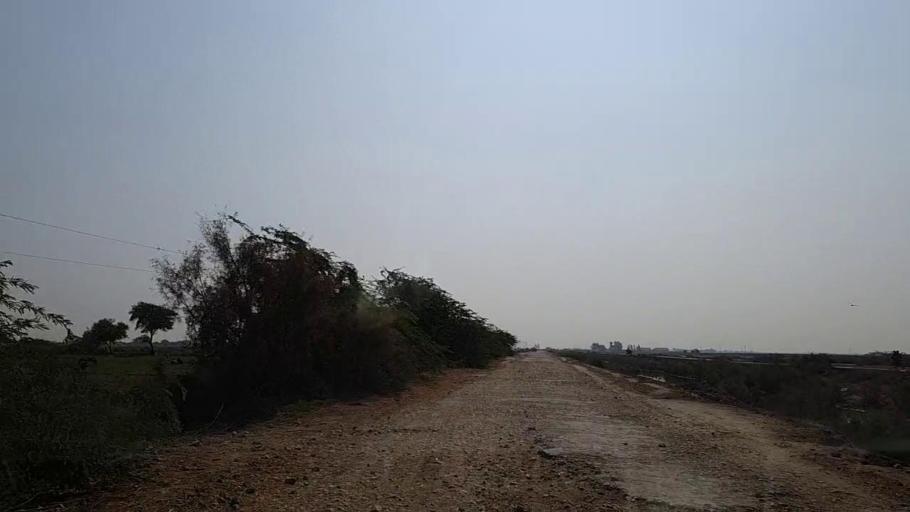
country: PK
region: Sindh
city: Thatta
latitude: 24.7185
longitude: 67.7684
